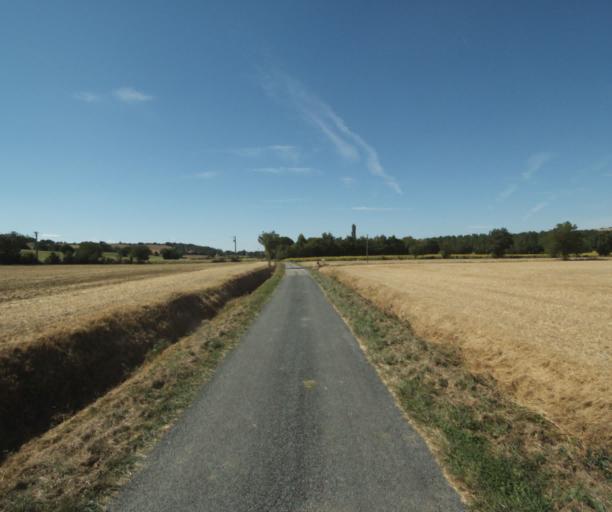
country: FR
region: Midi-Pyrenees
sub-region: Departement de la Haute-Garonne
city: Saint-Felix-Lauragais
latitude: 43.5043
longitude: 1.8940
